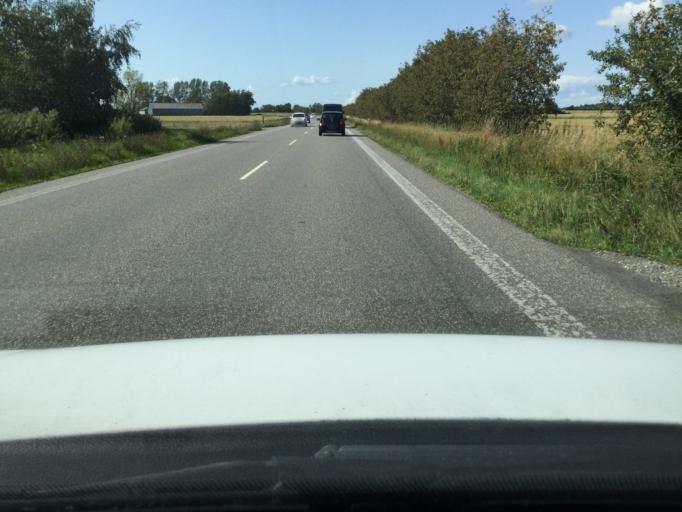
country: DK
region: Zealand
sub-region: Lolland Kommune
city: Nakskov
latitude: 54.8080
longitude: 11.2235
